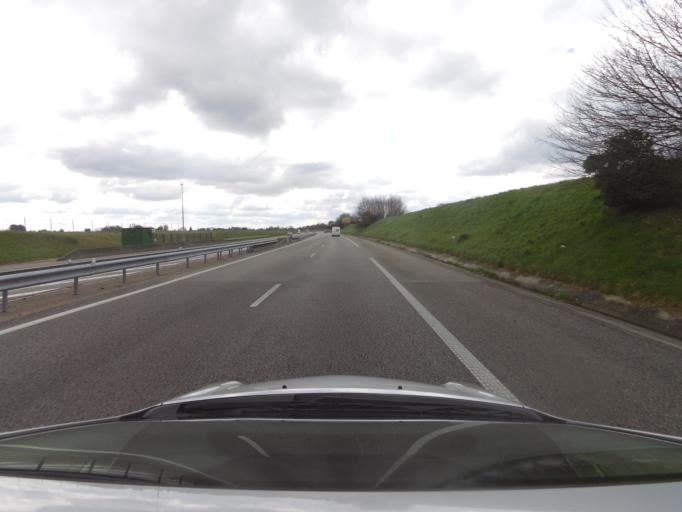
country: FR
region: Haute-Normandie
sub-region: Departement de la Seine-Maritime
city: Saint-Aubin-Routot
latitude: 49.5320
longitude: 0.3132
